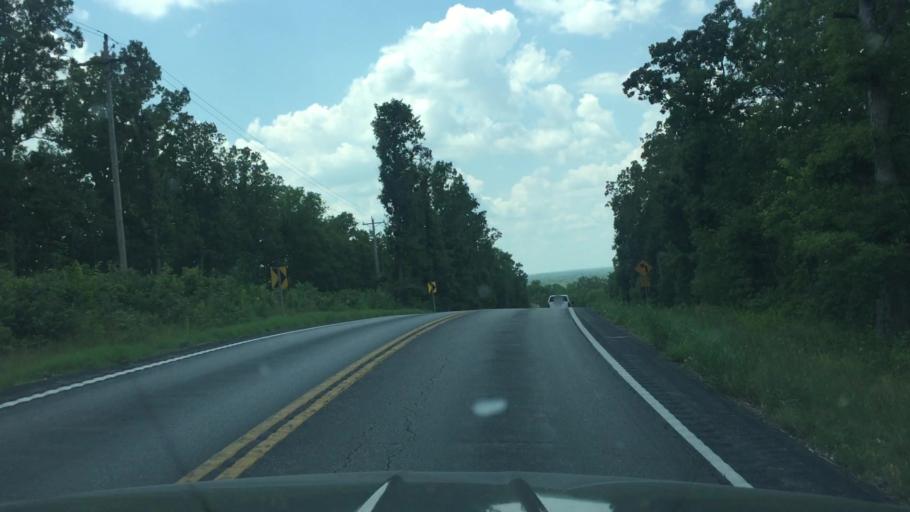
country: US
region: Missouri
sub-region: Miller County
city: Tuscumbia
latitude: 38.0959
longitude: -92.4966
